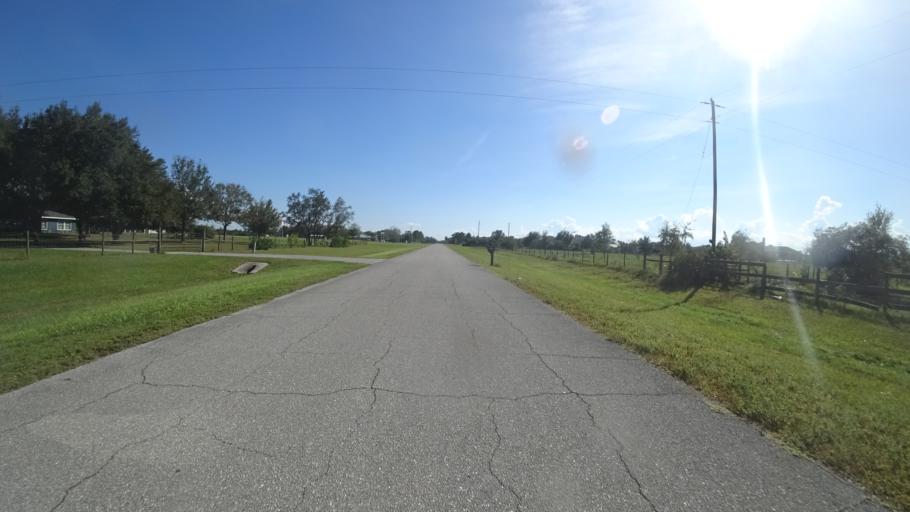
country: US
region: Florida
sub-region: Sarasota County
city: The Meadows
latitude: 27.4211
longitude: -82.2832
